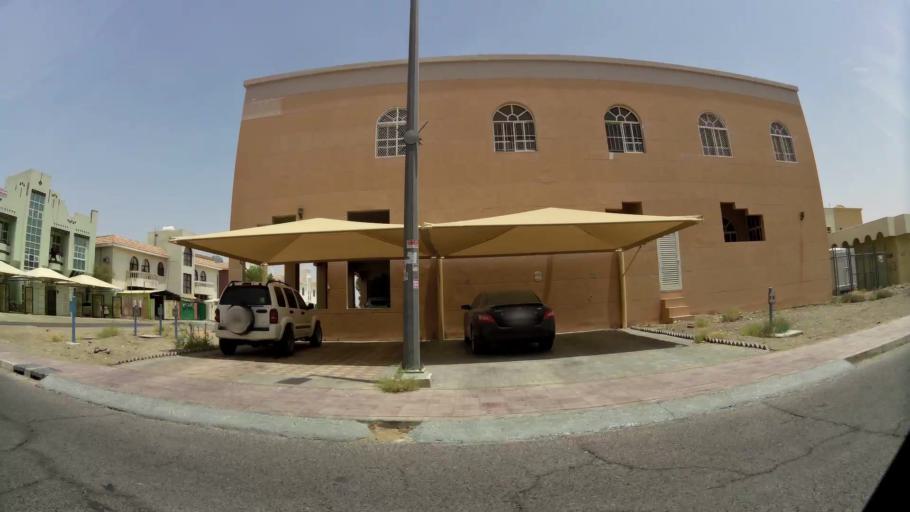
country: AE
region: Abu Dhabi
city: Al Ain
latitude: 24.2089
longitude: 55.7247
